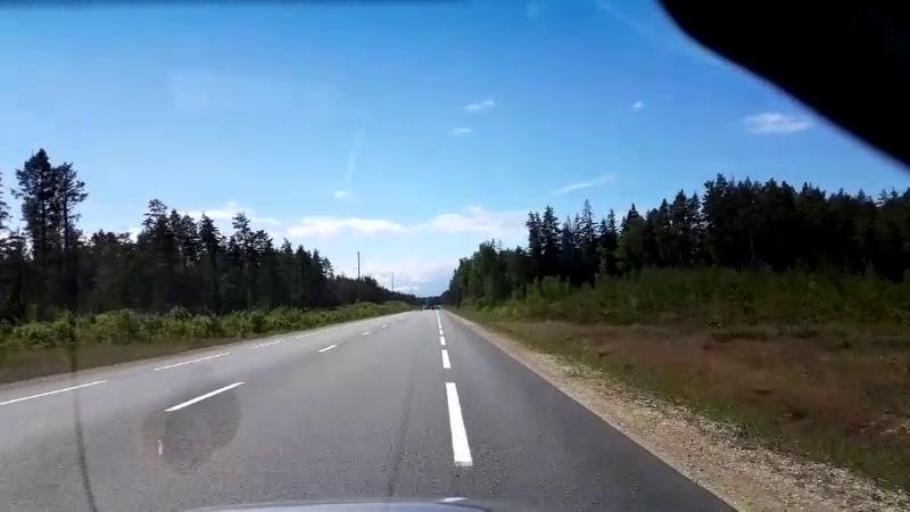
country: LV
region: Saulkrastu
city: Saulkrasti
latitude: 57.2051
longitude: 24.3822
